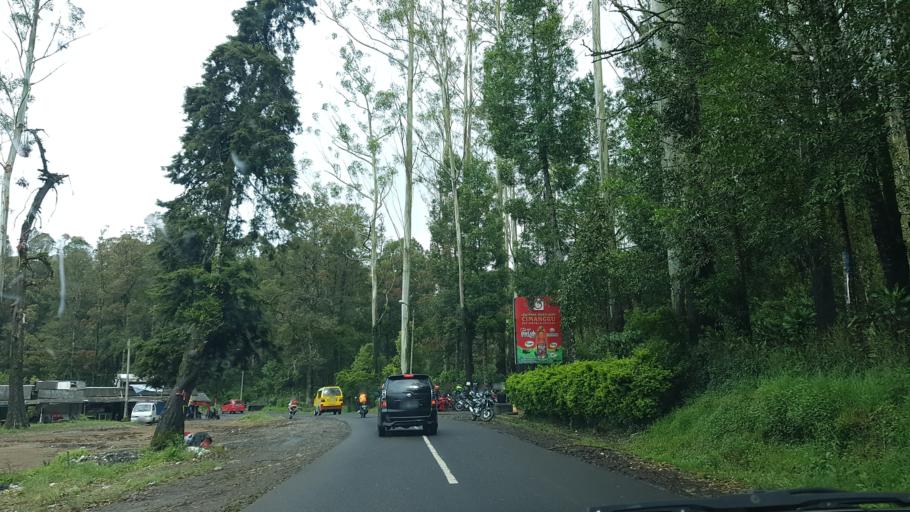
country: ID
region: West Java
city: Banjar
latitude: -7.1459
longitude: 107.3907
